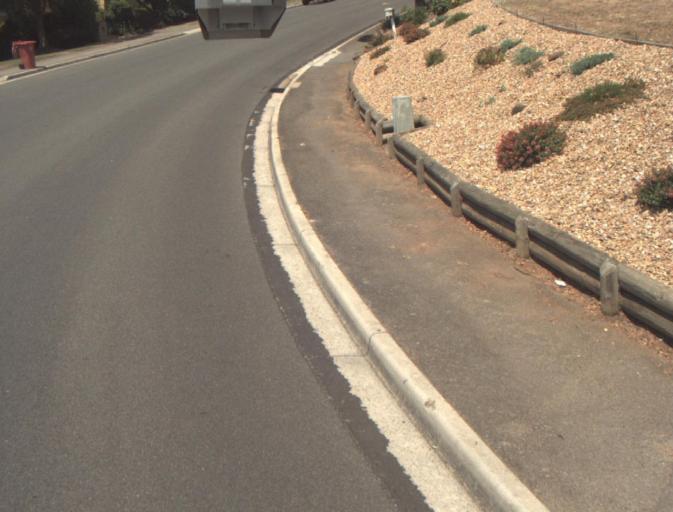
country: AU
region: Tasmania
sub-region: Launceston
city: Newstead
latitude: -41.4858
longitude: 147.1793
